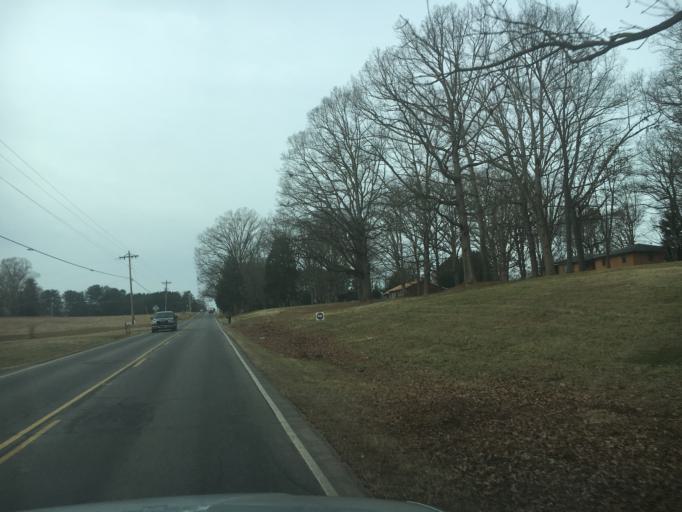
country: US
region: North Carolina
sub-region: Iredell County
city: Statesville
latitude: 35.8017
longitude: -80.8245
